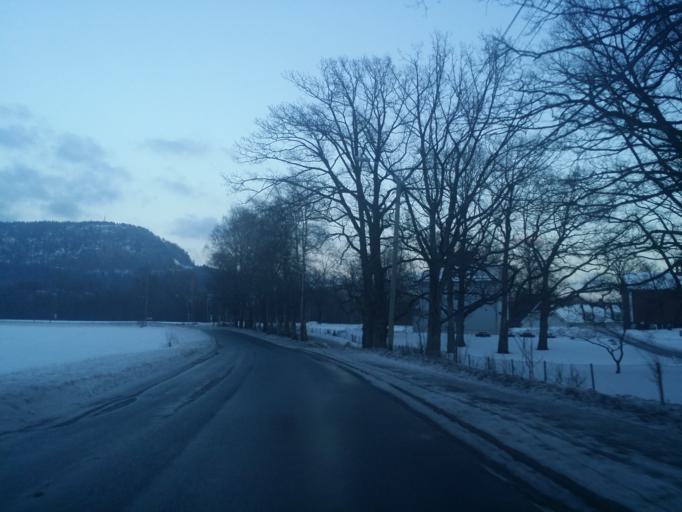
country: NO
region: Akershus
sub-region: Asker
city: Billingstad
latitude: 59.9124
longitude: 10.4842
